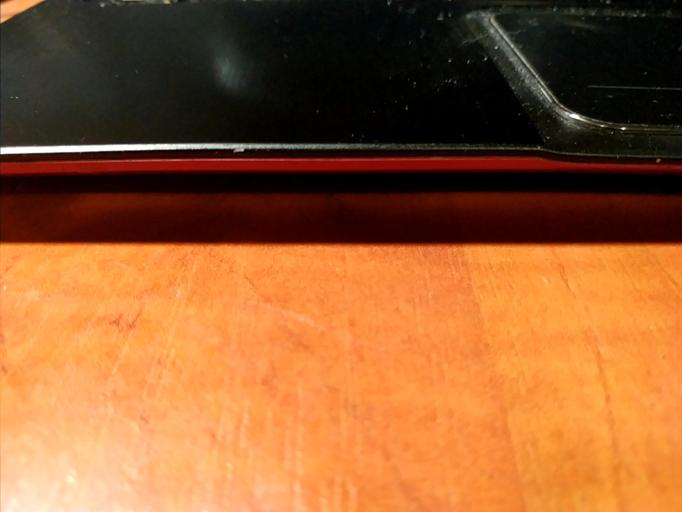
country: RU
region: Tverskaya
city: Ves'yegonsk
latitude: 58.7440
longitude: 37.5438
